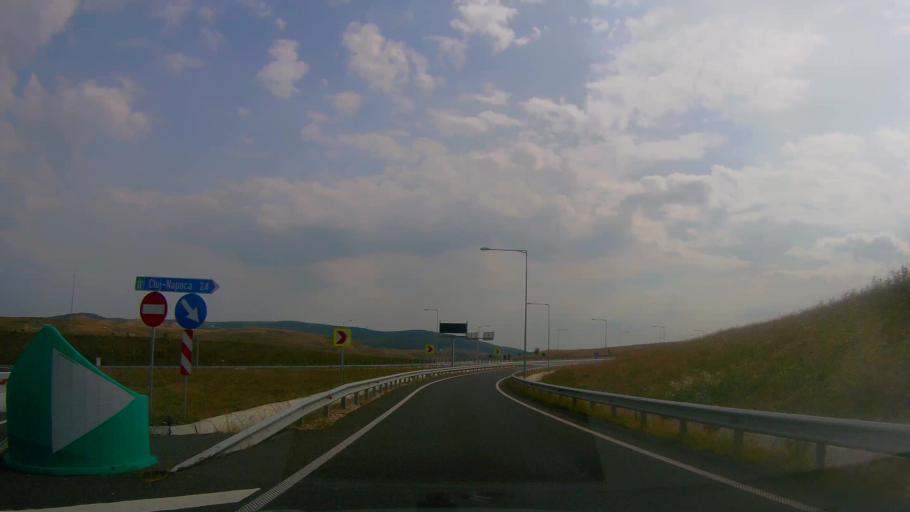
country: RO
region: Cluj
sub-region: Comuna Baciu
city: Mera
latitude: 46.8080
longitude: 23.4201
